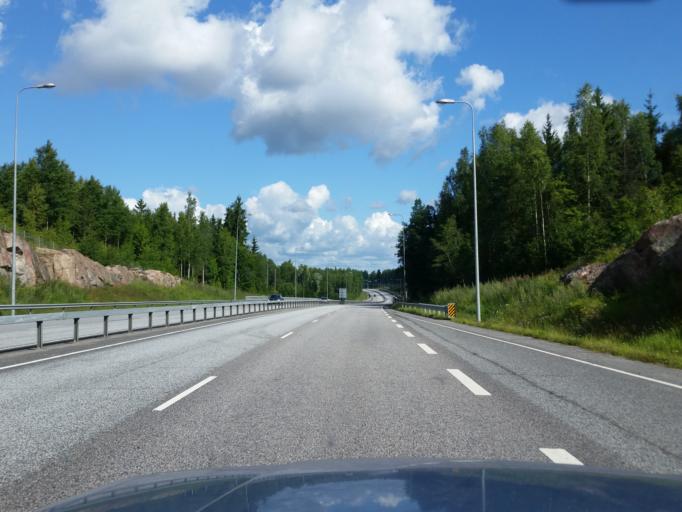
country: FI
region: Uusimaa
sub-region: Helsinki
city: Vihti
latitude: 60.3068
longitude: 24.3507
